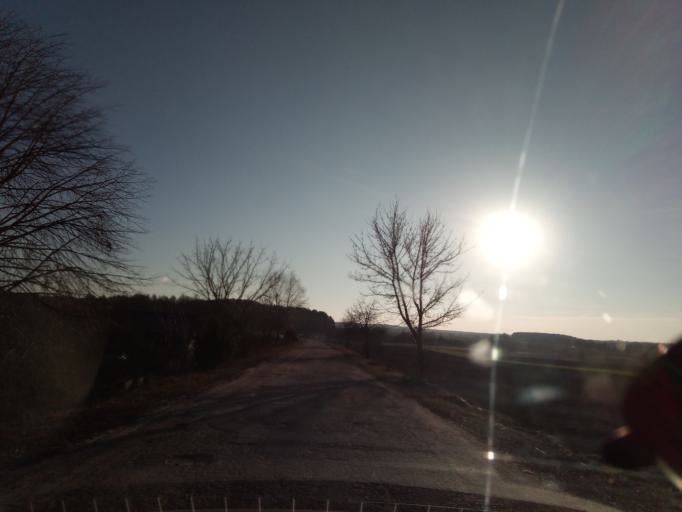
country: LT
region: Alytaus apskritis
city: Druskininkai
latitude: 53.9780
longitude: 23.9455
